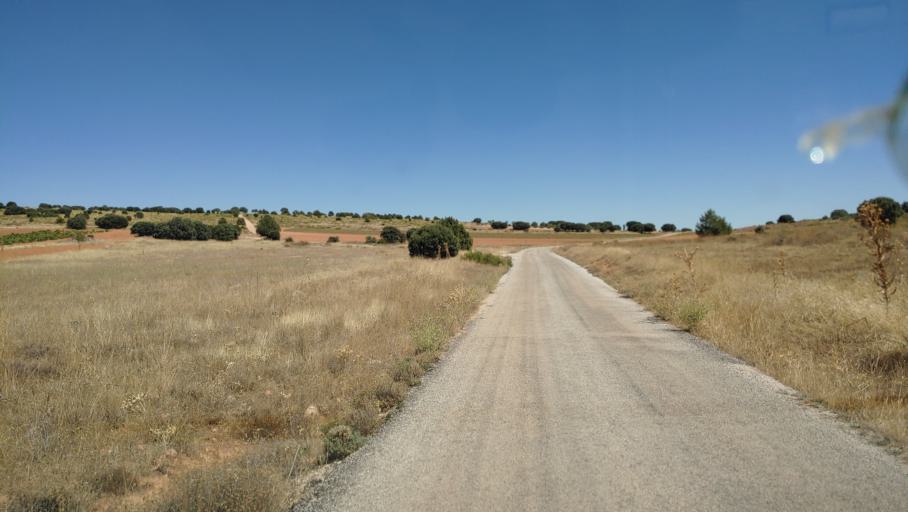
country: ES
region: Castille-La Mancha
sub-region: Provincia de Albacete
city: Ossa de Montiel
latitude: 38.9329
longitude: -2.7699
